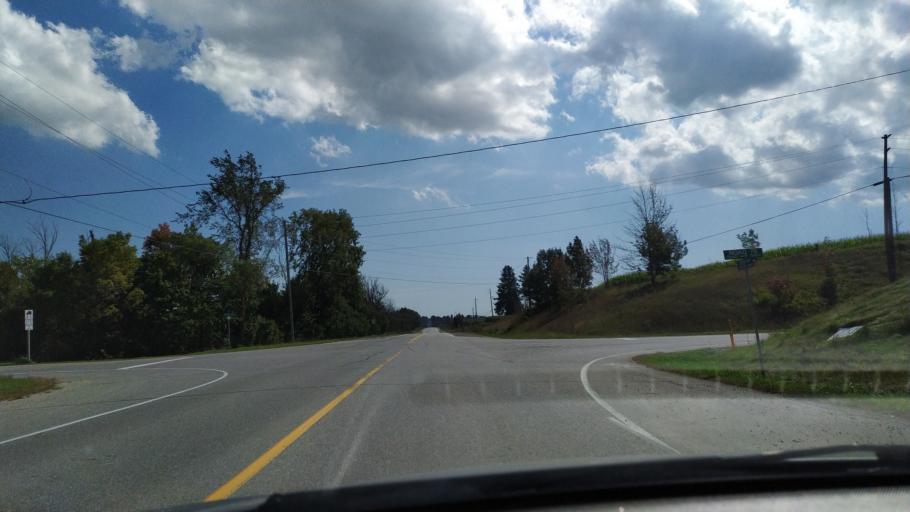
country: CA
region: Ontario
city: Ingersoll
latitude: 43.1496
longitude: -80.8981
